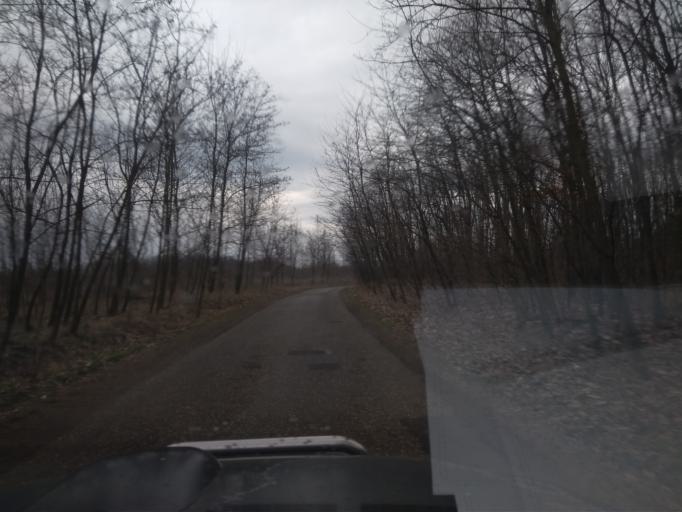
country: HU
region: Szabolcs-Szatmar-Bereg
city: Nyirpazony
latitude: 48.0151
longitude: 21.8101
